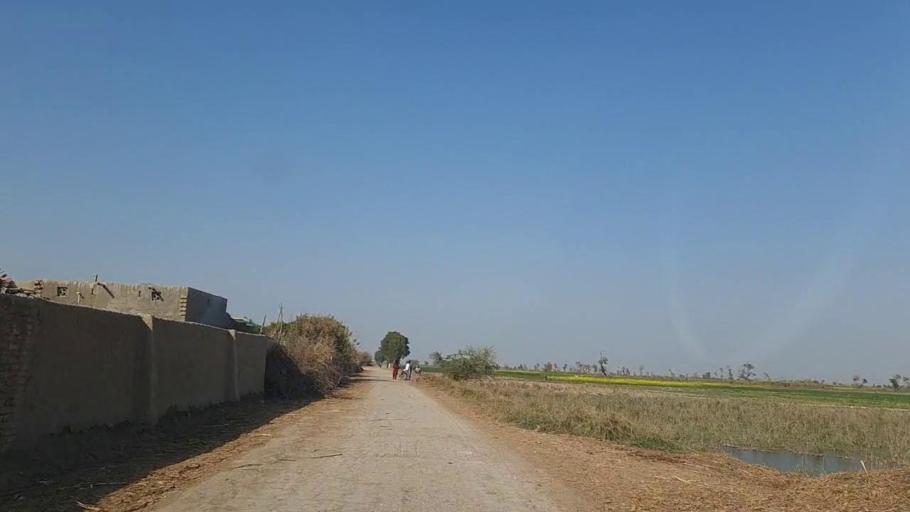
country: PK
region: Sindh
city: Daur
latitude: 26.4782
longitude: 68.2972
